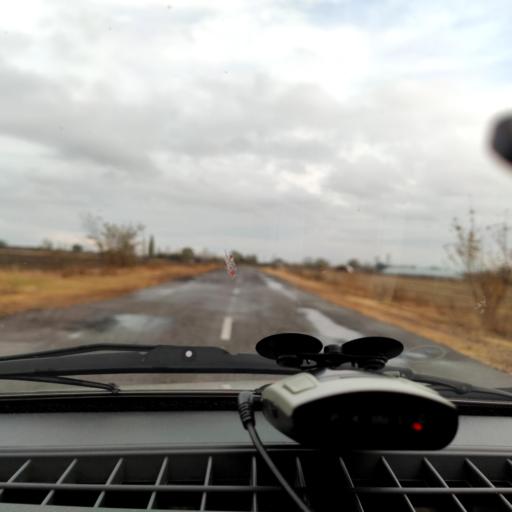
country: RU
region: Voronezj
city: Kolodeznyy
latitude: 51.2429
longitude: 39.0089
